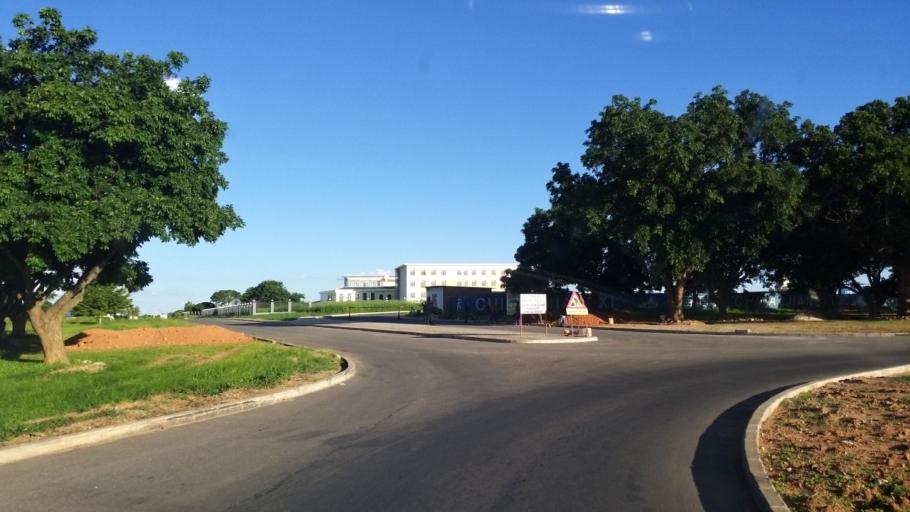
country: ZM
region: Lusaka
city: Lusaka
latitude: -15.3205
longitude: 28.4472
